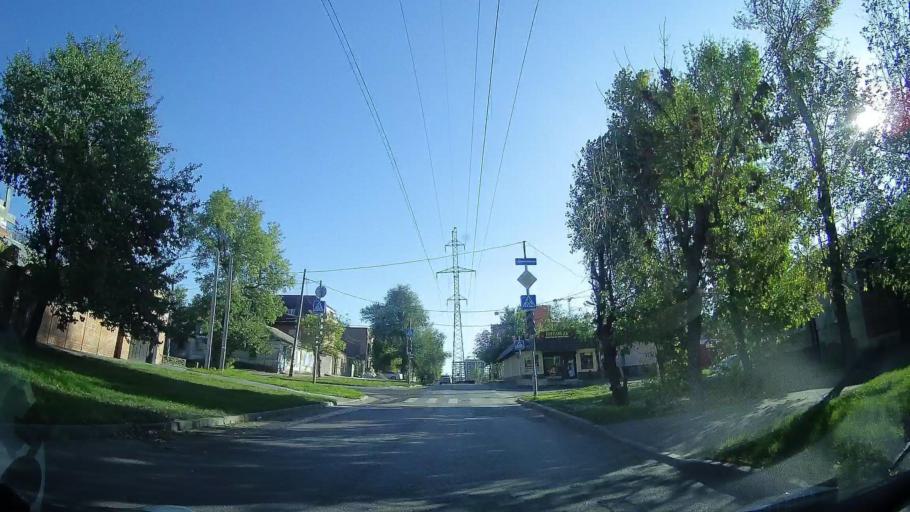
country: RU
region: Rostov
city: Rostov-na-Donu
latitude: 47.2302
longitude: 39.6899
